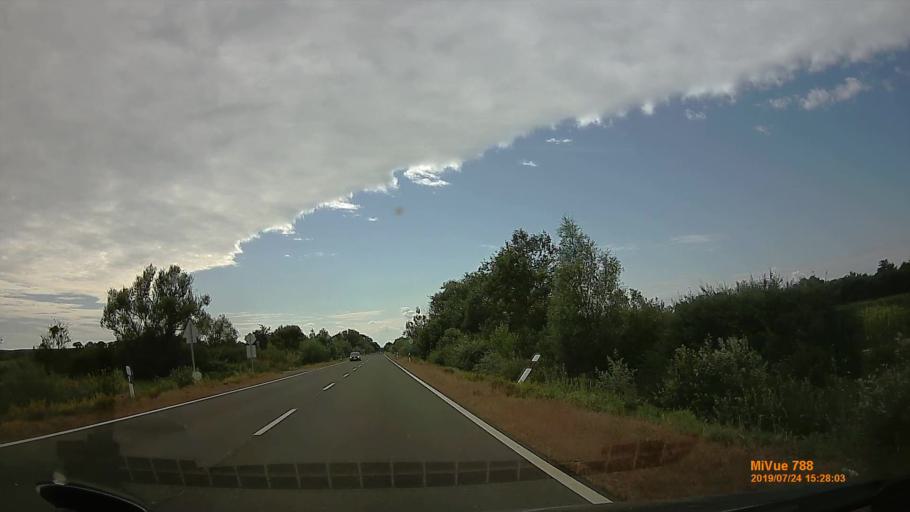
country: HU
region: Szabolcs-Szatmar-Bereg
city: Tarpa
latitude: 48.1608
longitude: 22.4863
